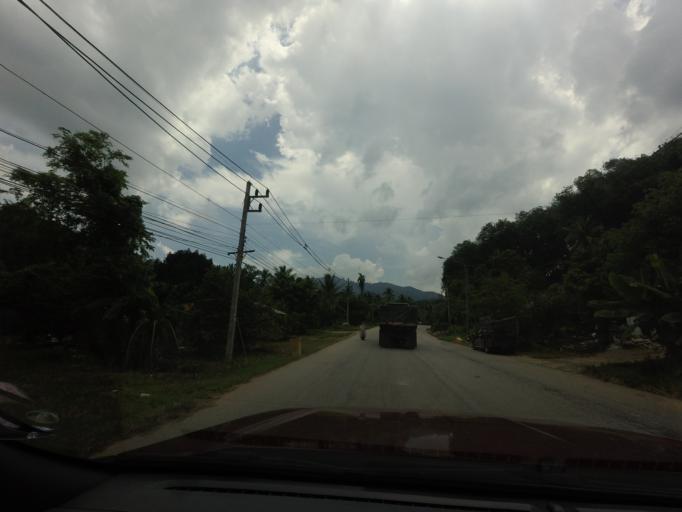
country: TH
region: Yala
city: Than To
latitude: 6.0715
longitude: 101.1944
